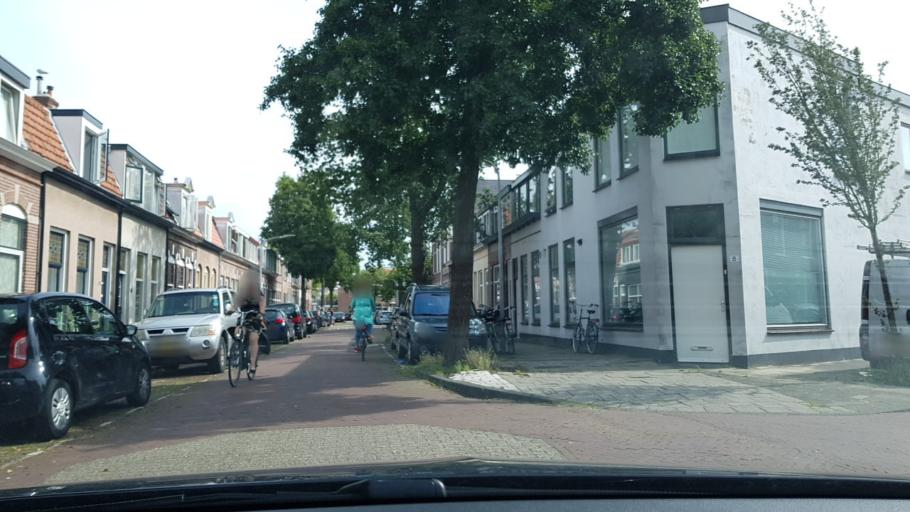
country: NL
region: North Holland
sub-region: Gemeente Haarlem
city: Haarlem
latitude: 52.3949
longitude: 4.6451
